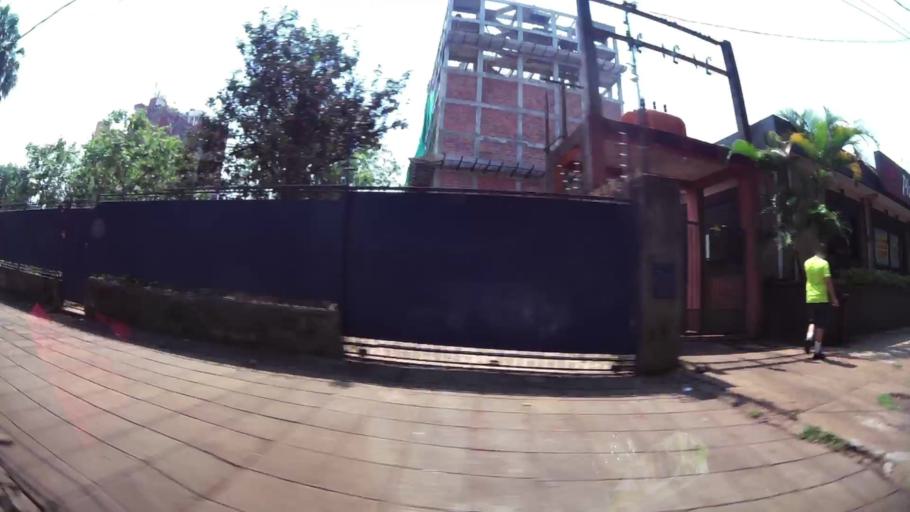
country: PY
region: Alto Parana
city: Ciudad del Este
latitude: -25.5163
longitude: -54.6141
